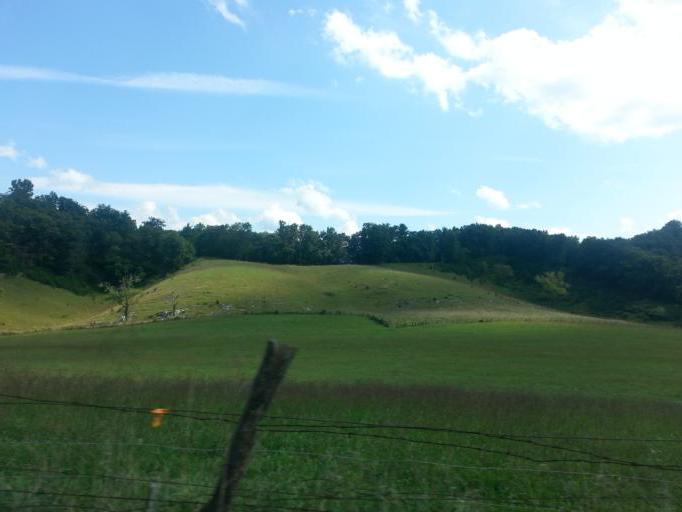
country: US
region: Virginia
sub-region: Washington County
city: Abingdon
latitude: 36.6715
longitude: -81.9543
